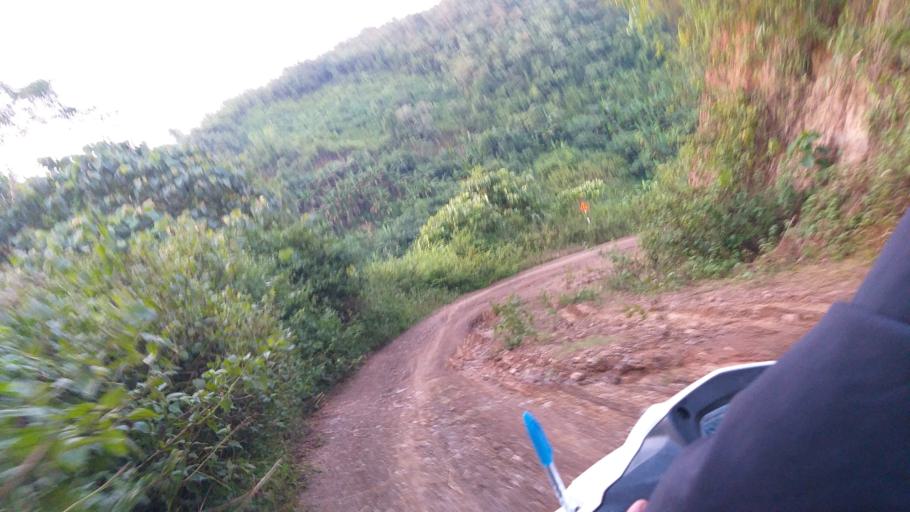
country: LA
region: Phongsali
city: Khoa
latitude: 21.4077
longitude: 102.6337
